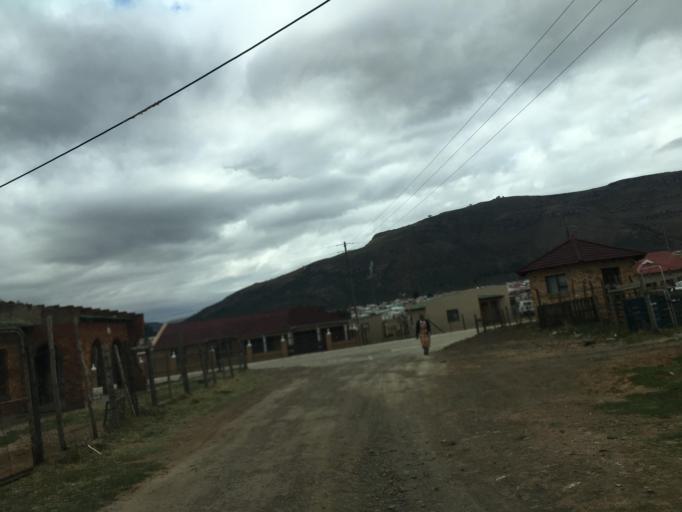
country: ZA
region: Eastern Cape
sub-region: Chris Hani District Municipality
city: Cala
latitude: -31.5377
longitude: 27.6973
